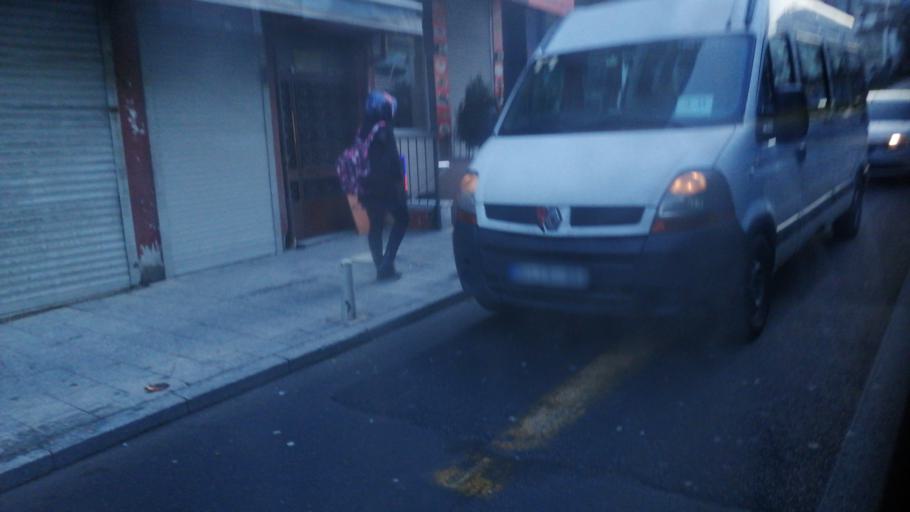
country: TR
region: Istanbul
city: Sisli
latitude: 41.0859
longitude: 28.9865
